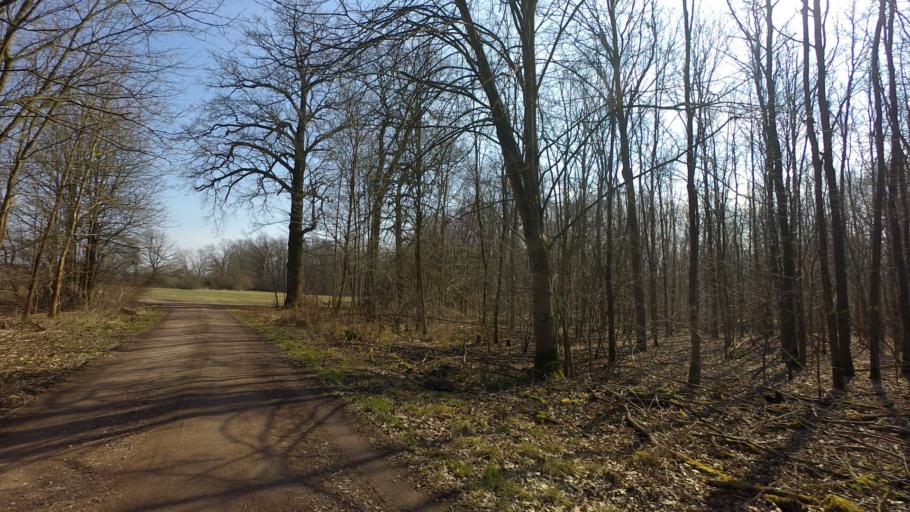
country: DE
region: Saxony-Anhalt
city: Vockerode
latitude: 51.8579
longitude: 12.3288
